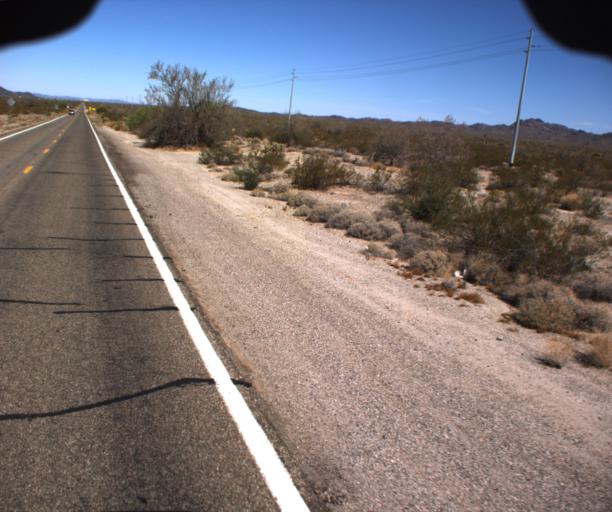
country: US
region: Arizona
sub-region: La Paz County
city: Salome
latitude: 33.7260
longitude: -113.7082
